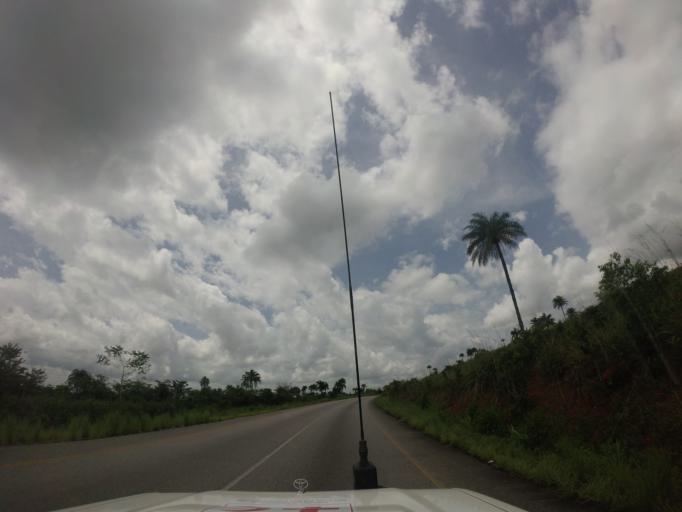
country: SL
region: Northern Province
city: Lunsar
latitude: 8.4669
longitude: -12.4864
